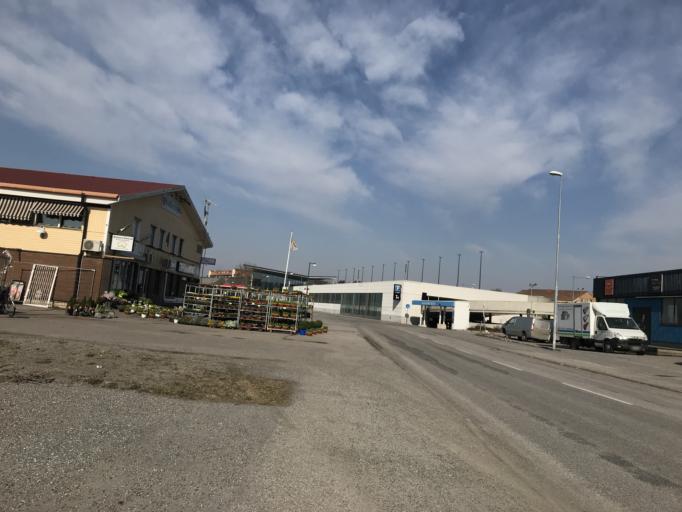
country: SE
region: Stockholm
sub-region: Osterakers Kommun
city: Akersberga
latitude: 59.4785
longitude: 18.3038
